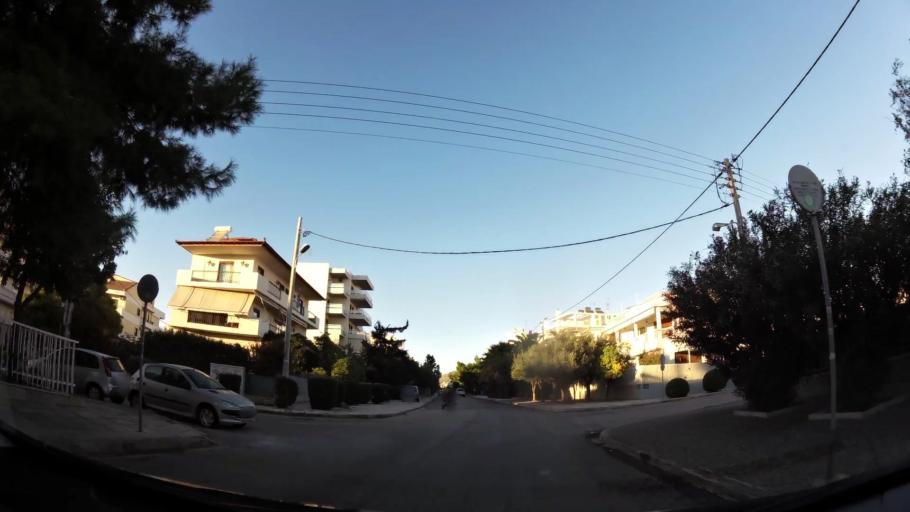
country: GR
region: Attica
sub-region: Nomarchia Athinas
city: Glyfada
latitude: 37.8764
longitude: 23.7521
